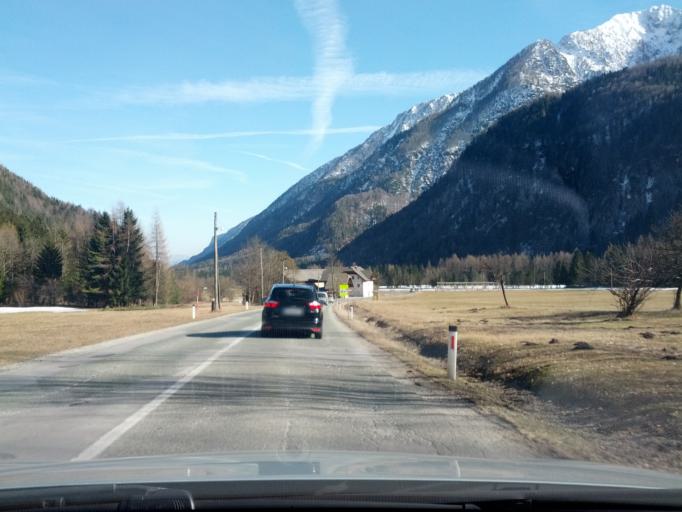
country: SI
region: Kranjska Gora
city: Mojstrana
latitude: 46.4839
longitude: 13.8468
